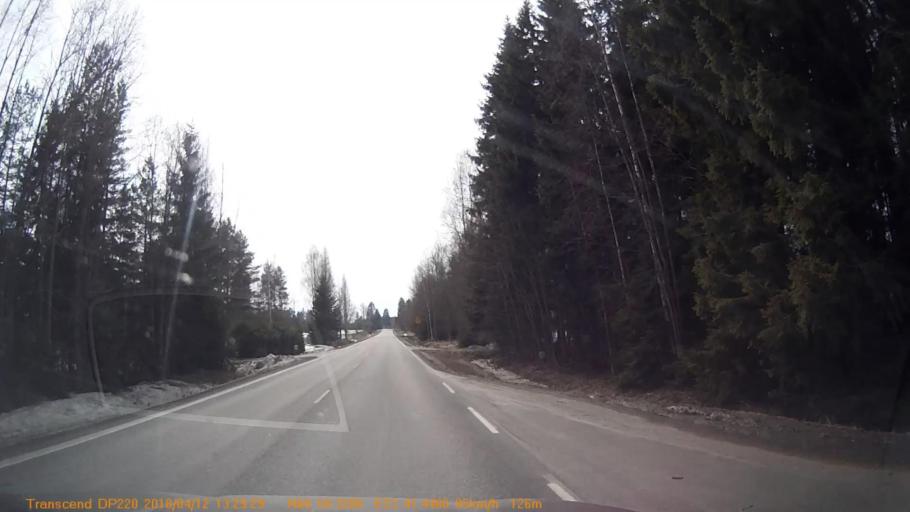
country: FI
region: Haeme
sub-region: Forssa
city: Forssa
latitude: 60.9720
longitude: 23.6905
